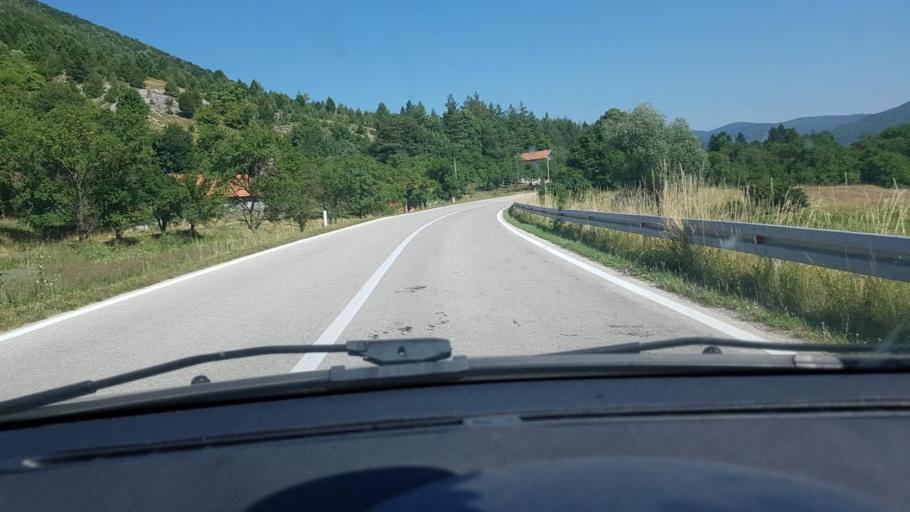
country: BA
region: Federation of Bosnia and Herzegovina
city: Bosansko Grahovo
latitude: 44.2580
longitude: 16.3038
